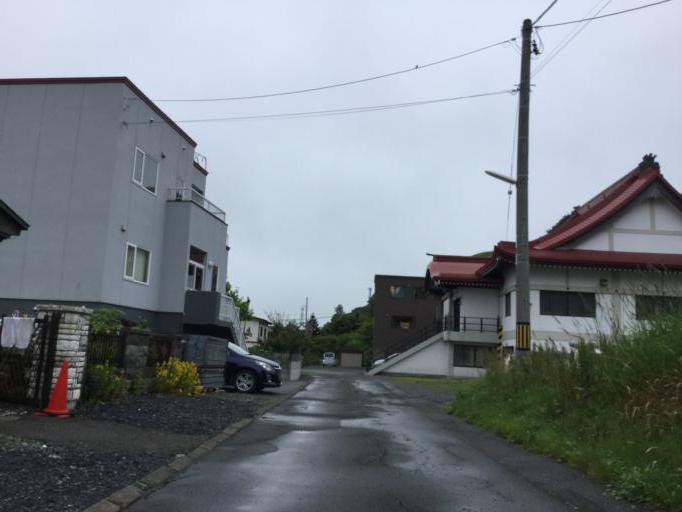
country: JP
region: Hokkaido
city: Wakkanai
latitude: 45.4004
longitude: 141.6761
